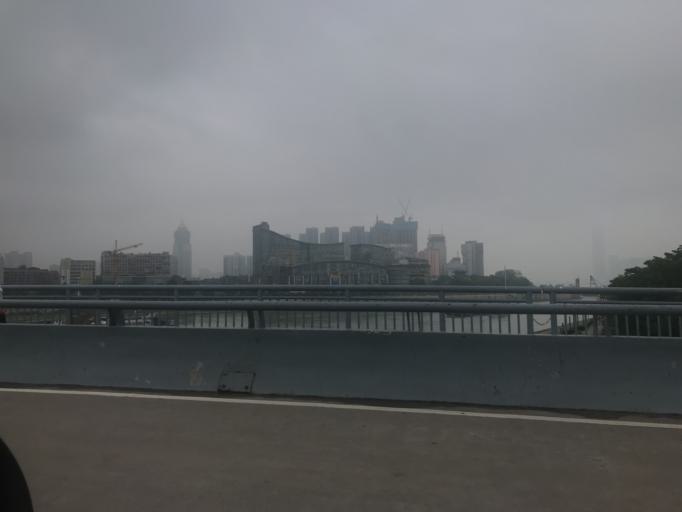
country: CN
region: Hubei
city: Wuhan
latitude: 30.5648
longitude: 114.2803
